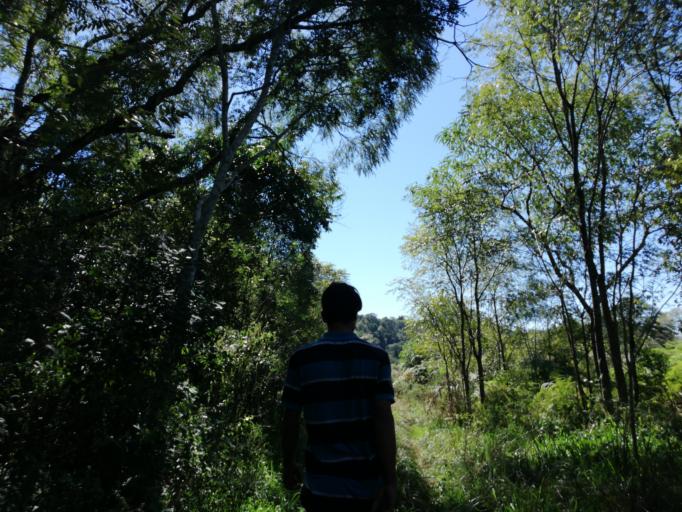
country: AR
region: Misiones
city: El Soberbio
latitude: -27.0612
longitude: -54.3757
